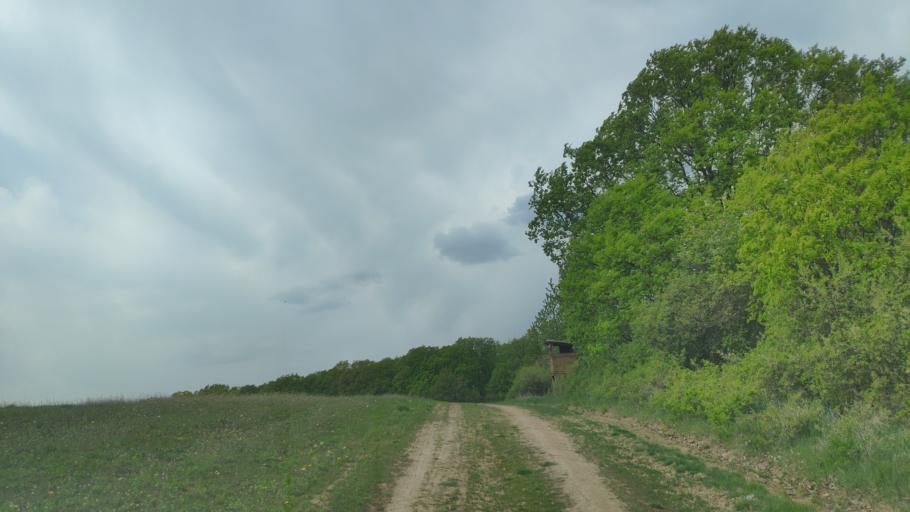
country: SK
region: Kosicky
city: Moldava nad Bodvou
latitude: 48.5613
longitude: 20.9412
